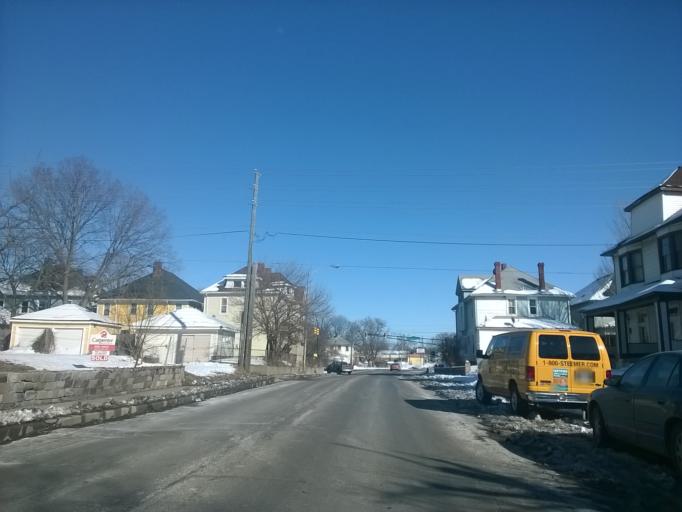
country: US
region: Indiana
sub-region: Marion County
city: Indianapolis
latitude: 39.7714
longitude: -86.1346
